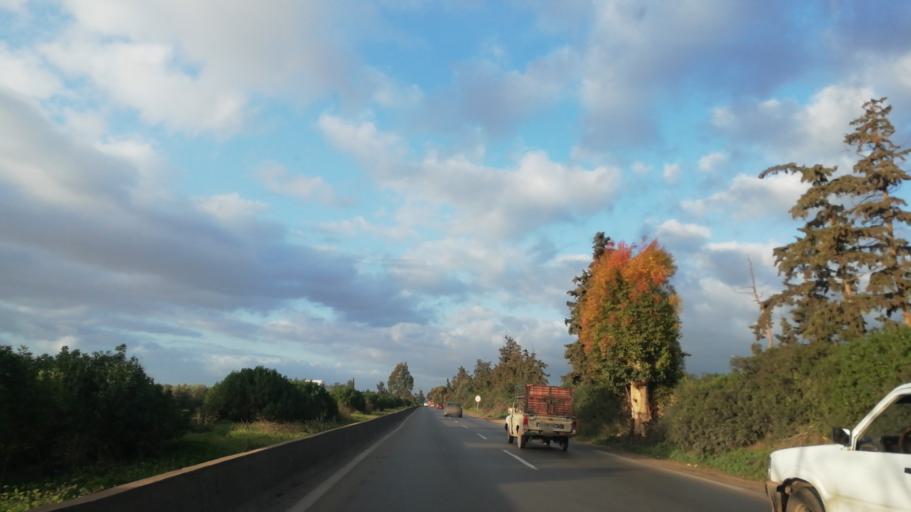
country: DZ
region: Oran
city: Bou Tlelis
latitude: 35.5976
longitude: -0.7794
